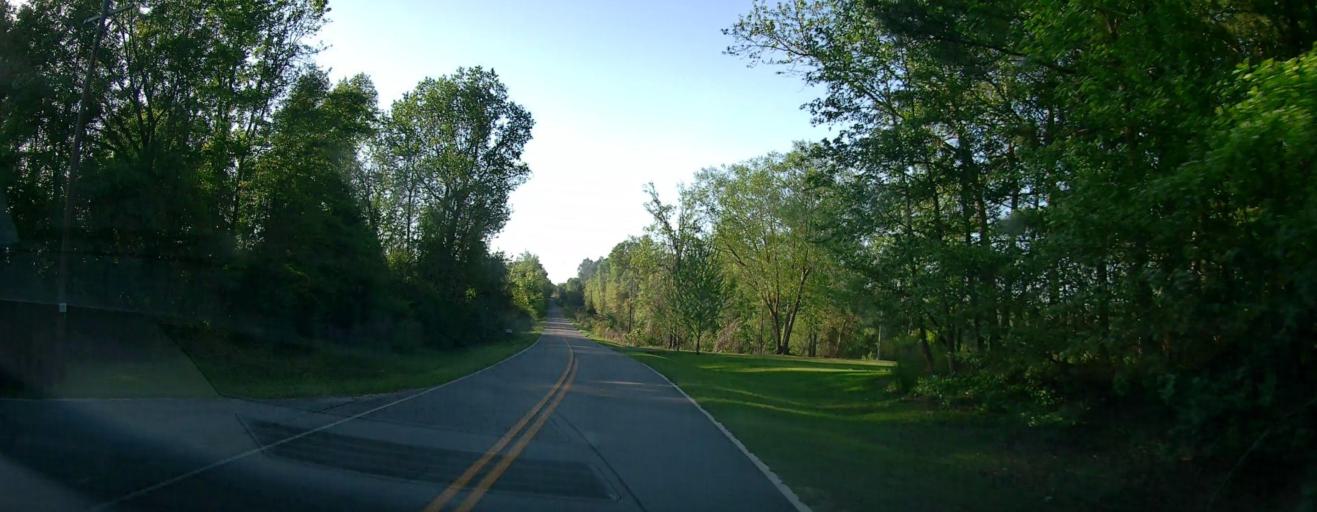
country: US
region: Georgia
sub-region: Macon County
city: Oglethorpe
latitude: 32.2732
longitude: -84.0858
